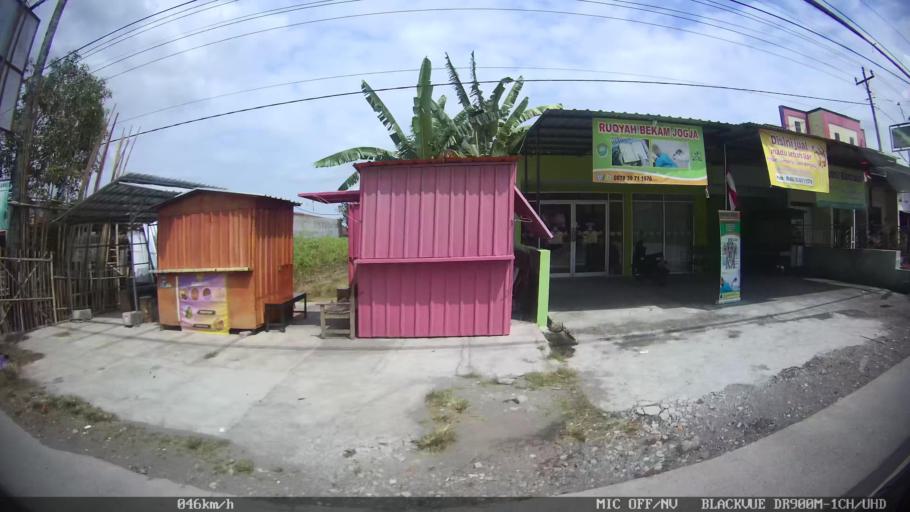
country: ID
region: Central Java
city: Candi Prambanan
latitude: -7.7917
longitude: 110.4827
